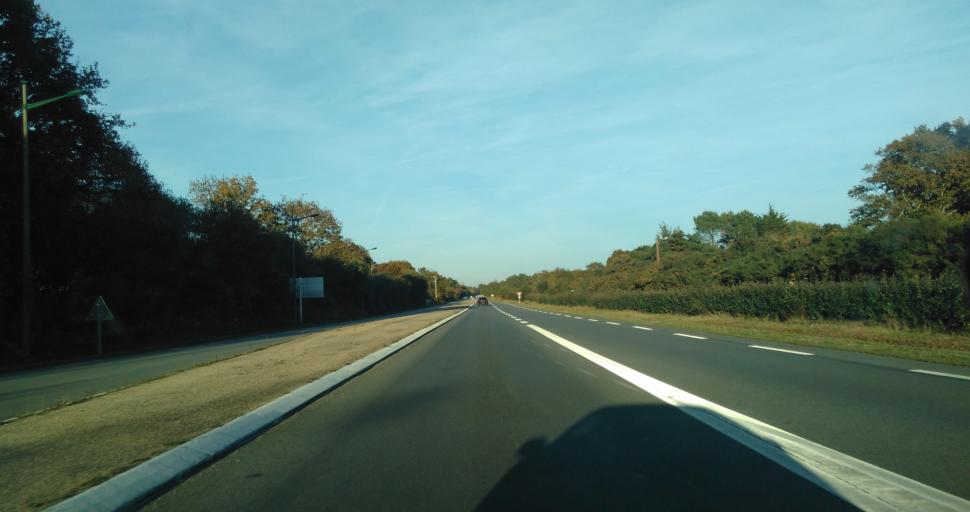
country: FR
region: Brittany
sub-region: Departement du Morbihan
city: Ploemel
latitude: 47.6270
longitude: -3.0672
